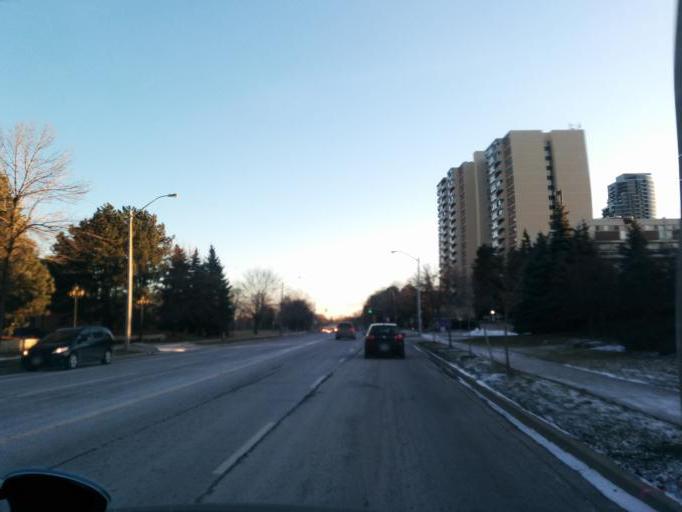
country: CA
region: Ontario
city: Etobicoke
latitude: 43.6445
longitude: -79.5589
